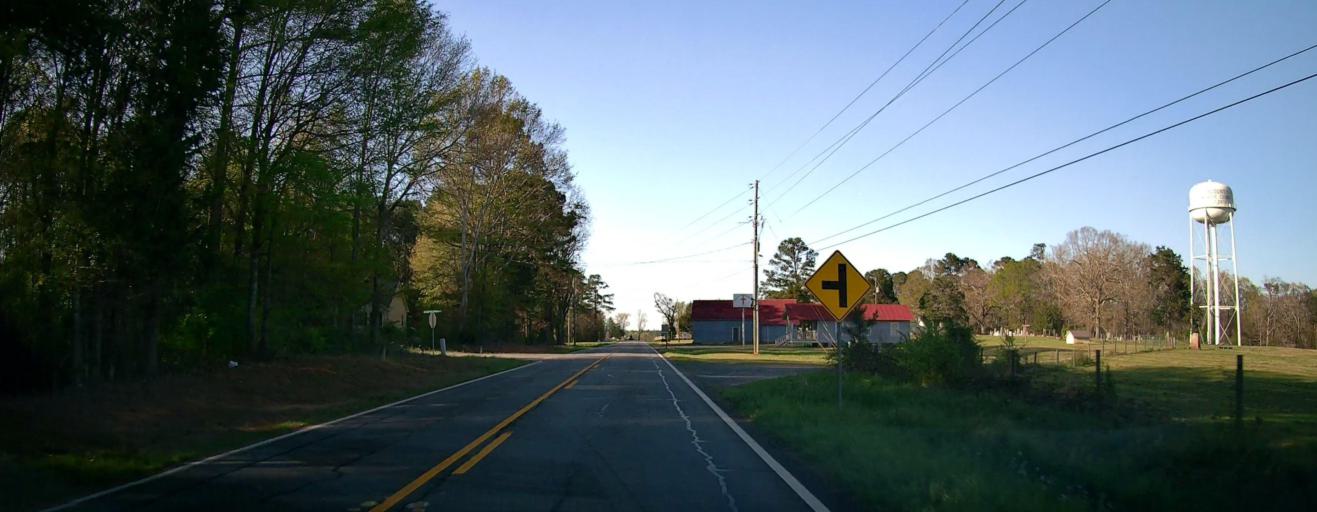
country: US
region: Georgia
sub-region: Butts County
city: Indian Springs
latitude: 33.1756
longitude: -83.9589
